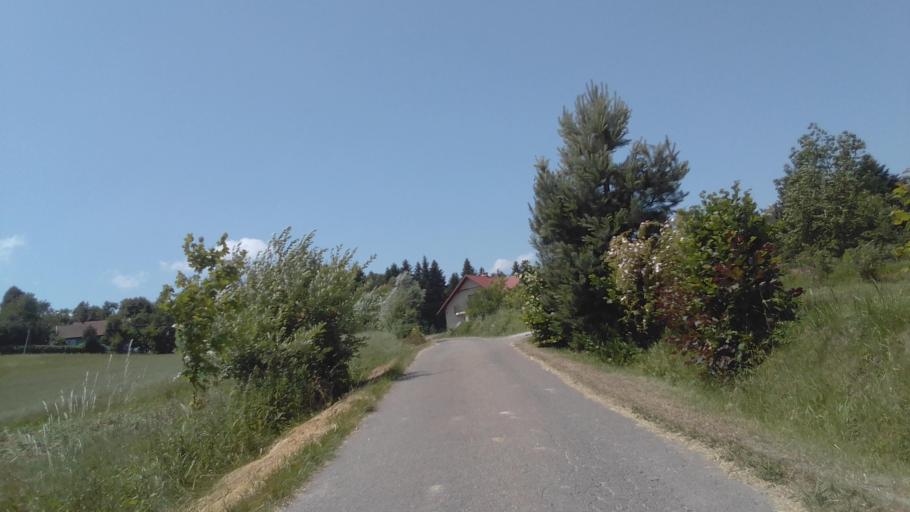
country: PL
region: Subcarpathian Voivodeship
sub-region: Powiat strzyzowski
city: Strzyzow
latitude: 49.8618
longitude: 21.7622
